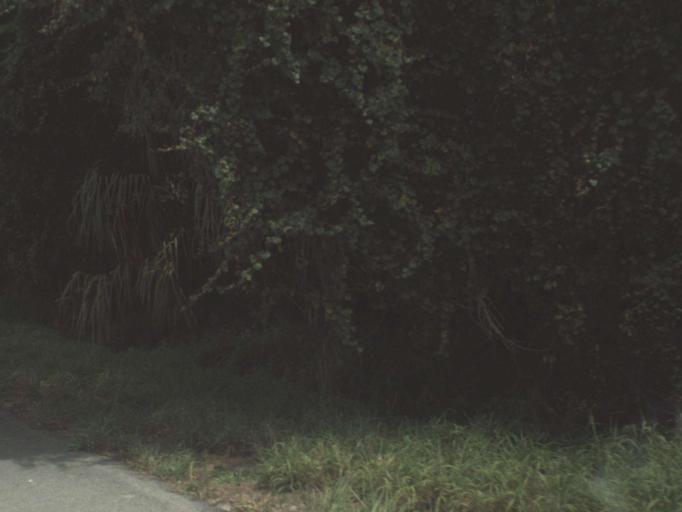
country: US
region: Florida
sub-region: Martin County
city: Indiantown
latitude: 27.0282
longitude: -80.6334
